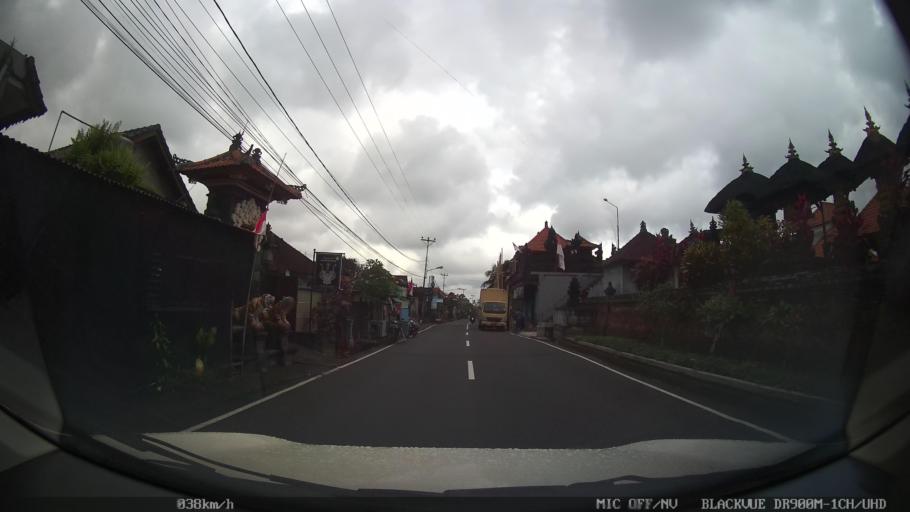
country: ID
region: Bali
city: Banjar Sayanbaleran
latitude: -8.5209
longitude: 115.1868
